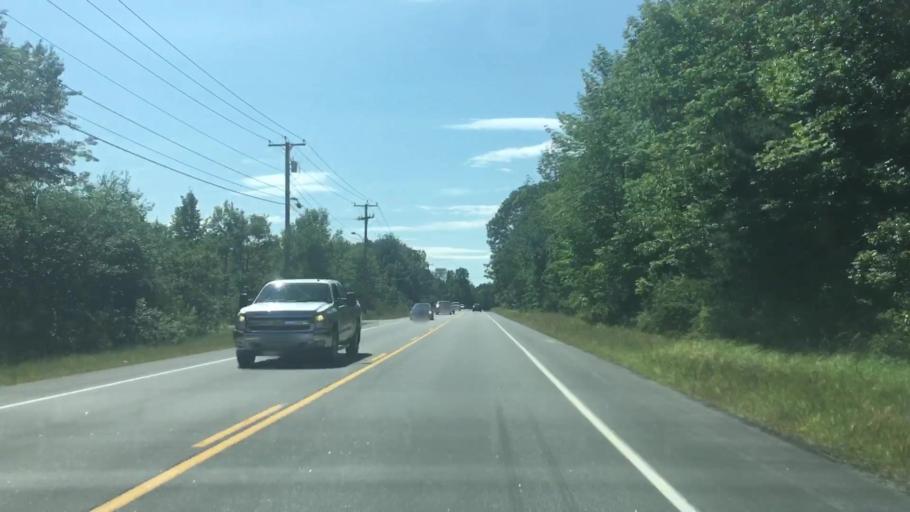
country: US
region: Maine
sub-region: Androscoggin County
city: Sabattus
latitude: 44.1255
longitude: -70.0747
